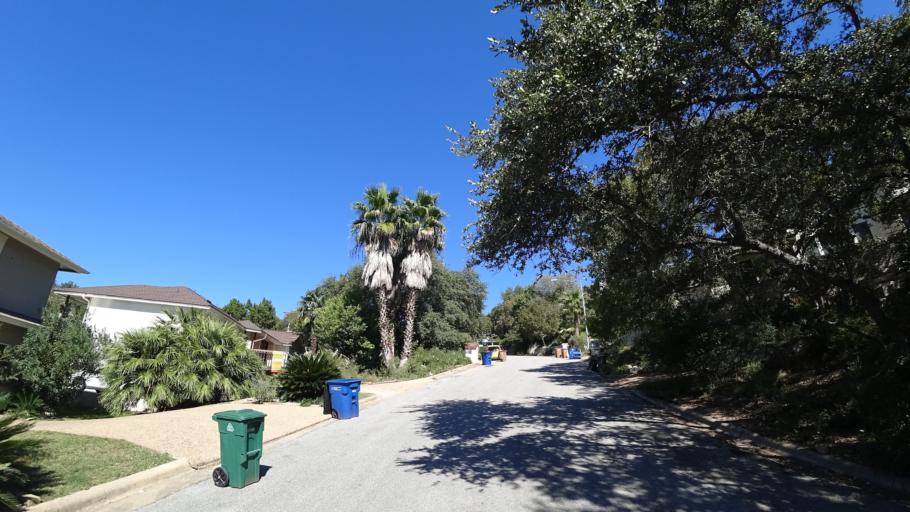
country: US
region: Texas
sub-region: Travis County
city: West Lake Hills
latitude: 30.3493
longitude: -97.7808
